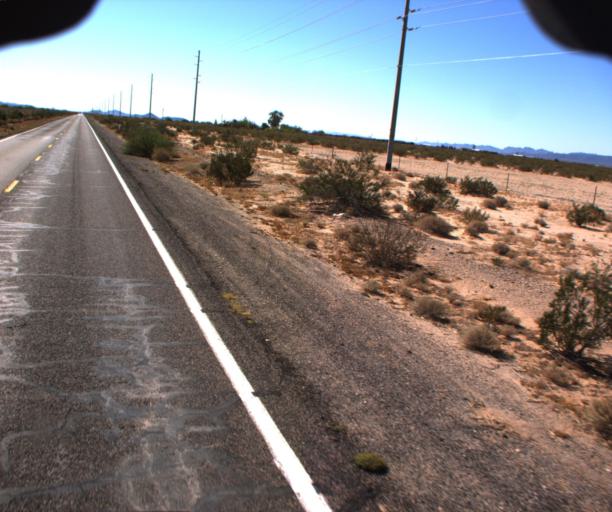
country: US
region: Arizona
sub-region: La Paz County
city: Salome
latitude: 33.8616
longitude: -113.9191
